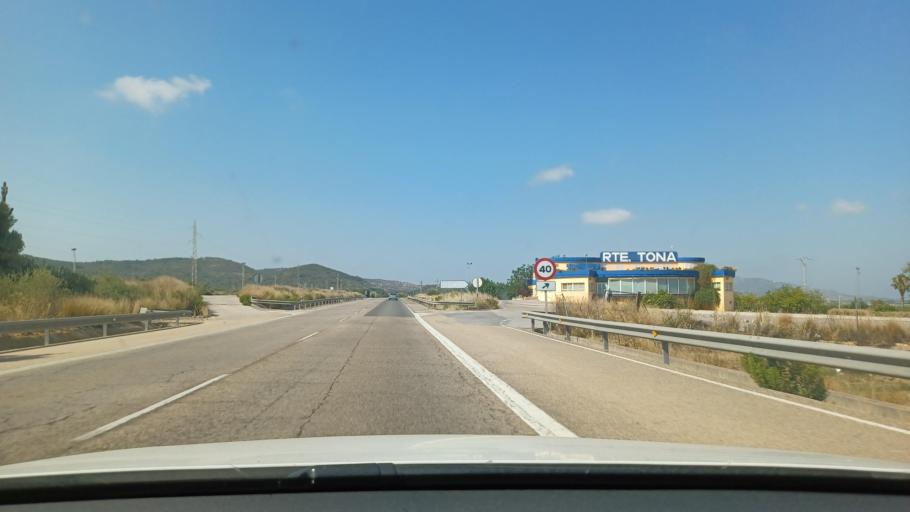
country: ES
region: Valencia
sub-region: Provincia de Castello
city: Torreblanca
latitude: 40.2008
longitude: 0.1781
